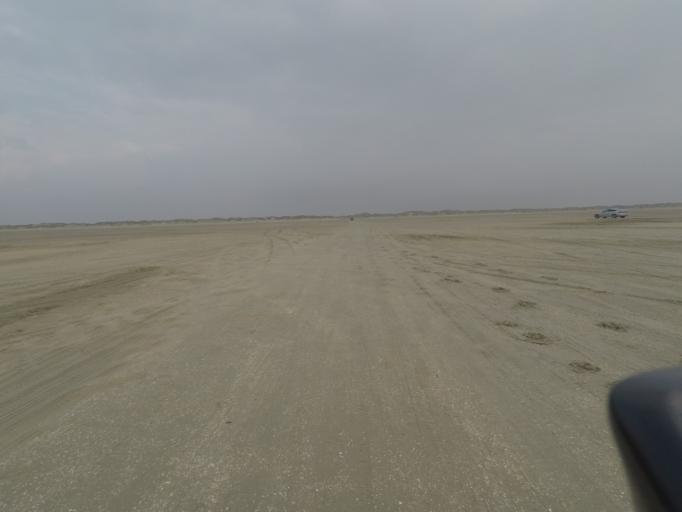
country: DE
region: Schleswig-Holstein
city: List
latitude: 55.1472
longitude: 8.4811
